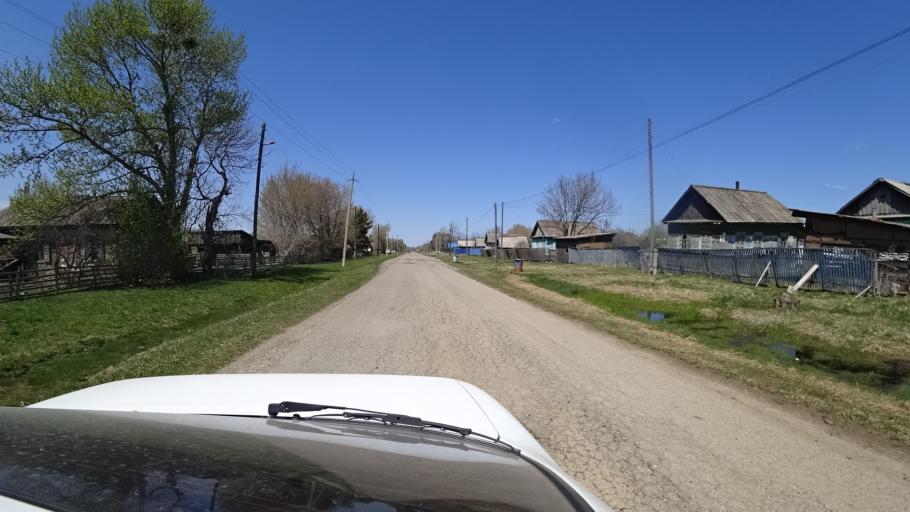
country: RU
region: Primorskiy
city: Lazo
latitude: 45.7918
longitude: 133.7672
